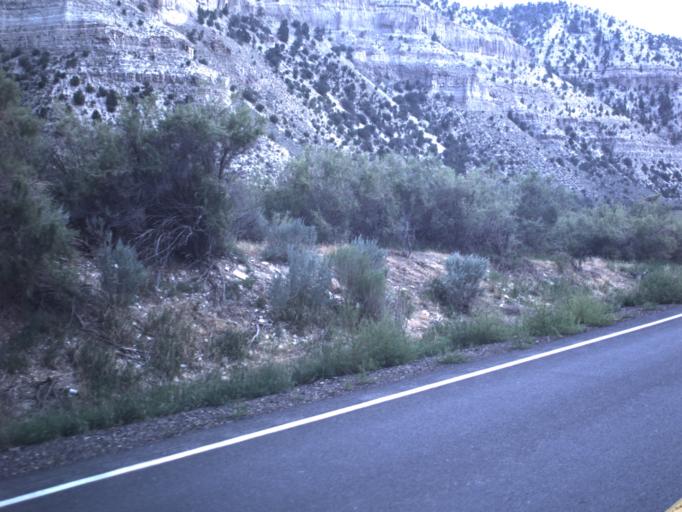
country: US
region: Utah
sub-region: Duchesne County
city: Duchesne
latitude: 40.0860
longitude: -110.4967
